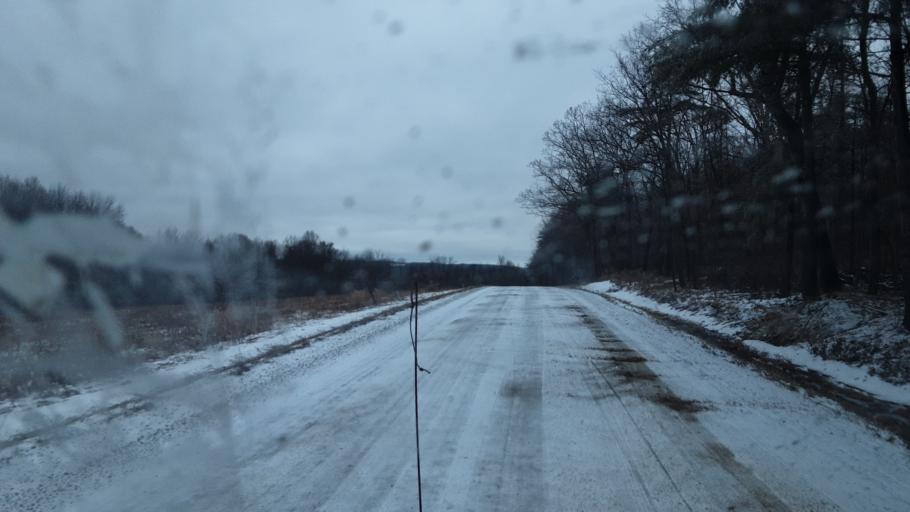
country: US
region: New York
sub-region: Allegany County
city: Friendship
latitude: 42.2793
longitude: -78.1622
